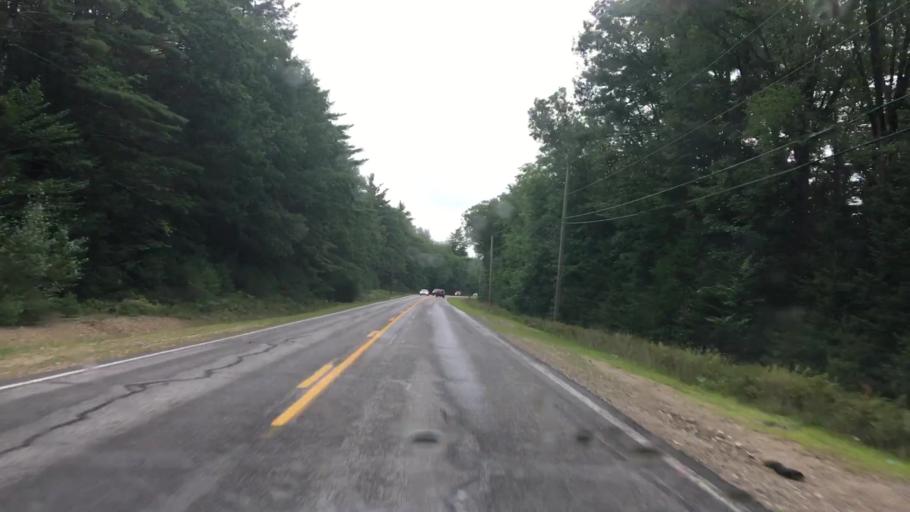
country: US
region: Maine
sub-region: Oxford County
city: Fryeburg
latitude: 43.9964
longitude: -70.9404
